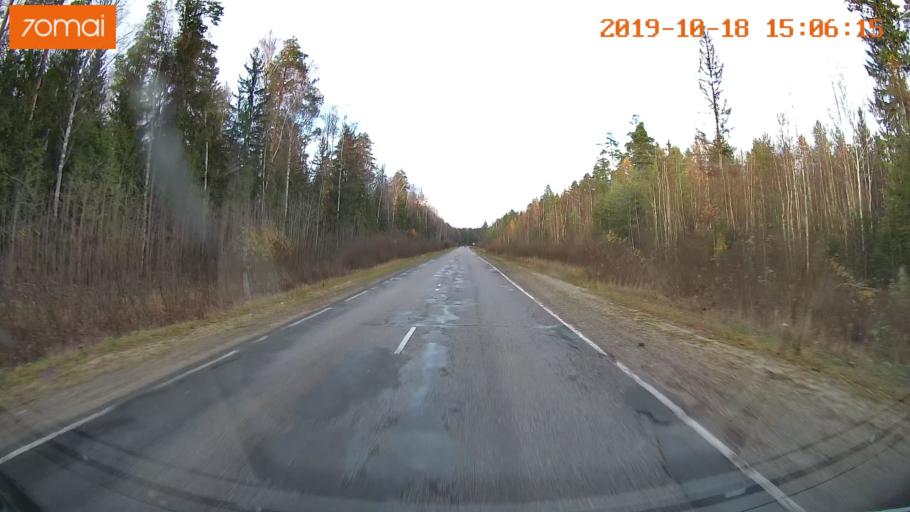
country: RU
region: Vladimir
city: Gus'-Khrustal'nyy
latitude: 55.5272
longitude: 40.5772
